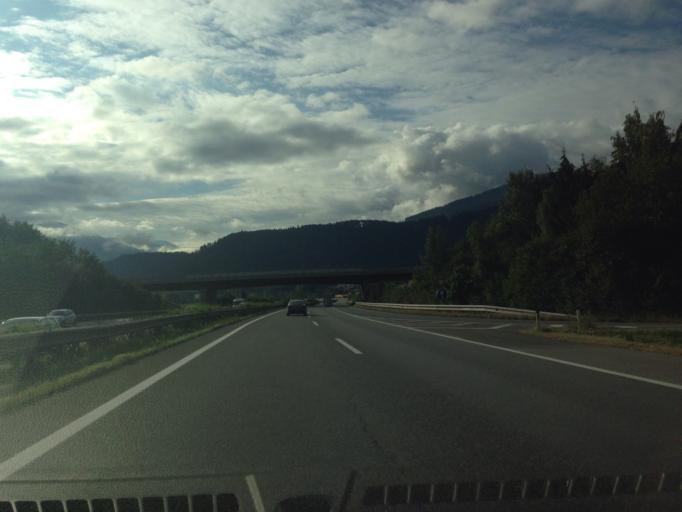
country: AT
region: Tyrol
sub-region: Politischer Bezirk Innsbruck Land
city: Vols
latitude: 47.2615
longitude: 11.3216
